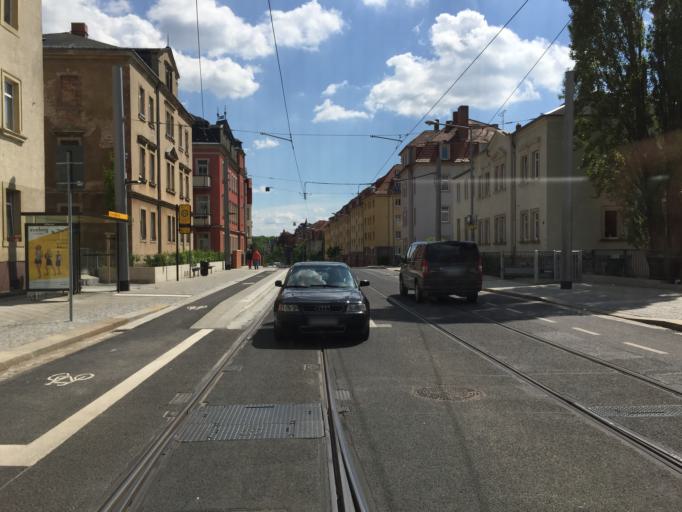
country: DE
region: Saxony
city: Dresden
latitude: 51.0489
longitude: 13.6921
